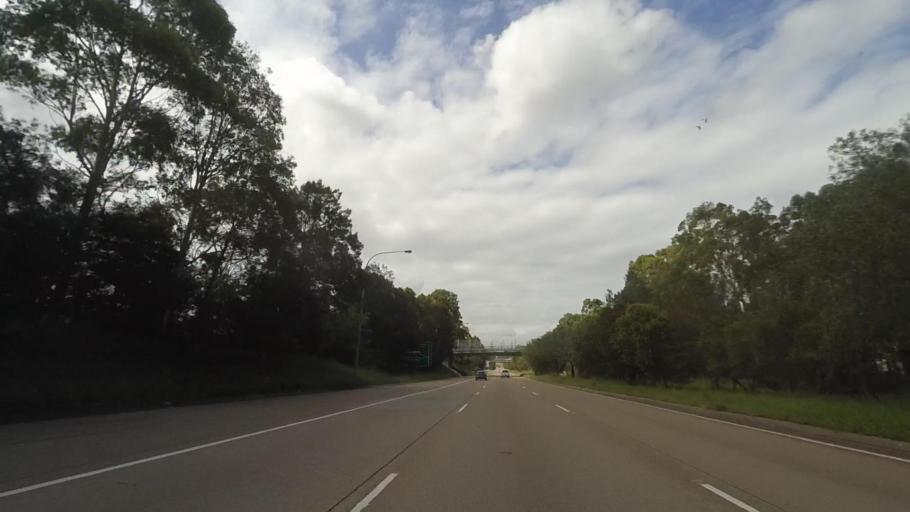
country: AU
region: New South Wales
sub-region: Newcastle
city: North Lambton
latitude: -32.9023
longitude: 151.6935
